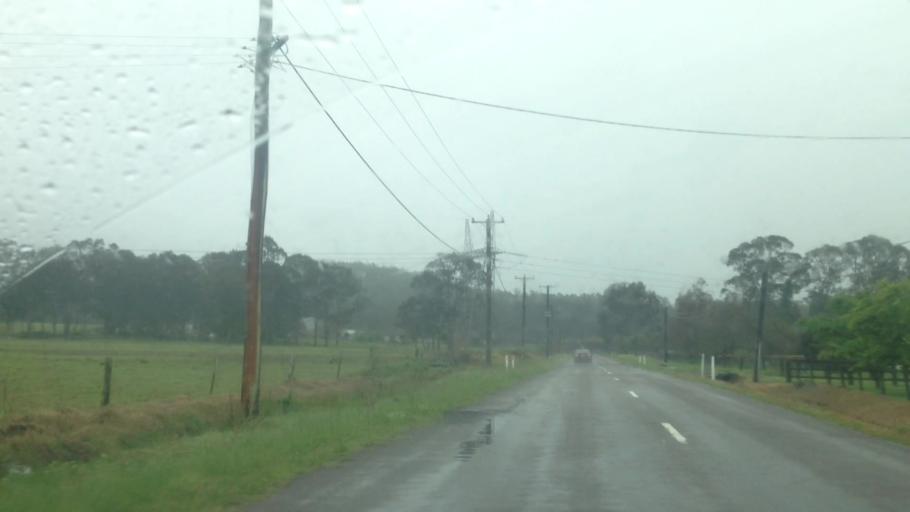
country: AU
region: New South Wales
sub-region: Wyong Shire
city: Little Jilliby
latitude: -33.2197
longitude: 151.3725
